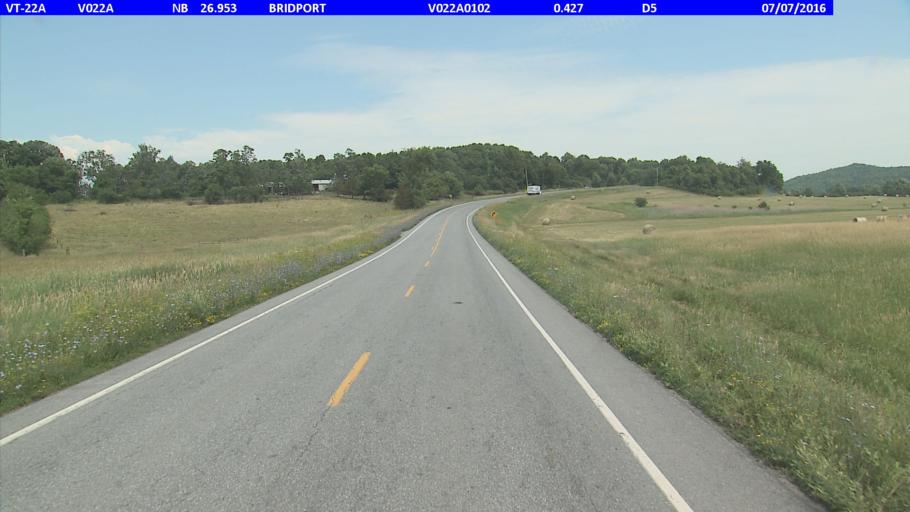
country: US
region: New York
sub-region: Essex County
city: Ticonderoga
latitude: 43.9470
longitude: -73.3125
